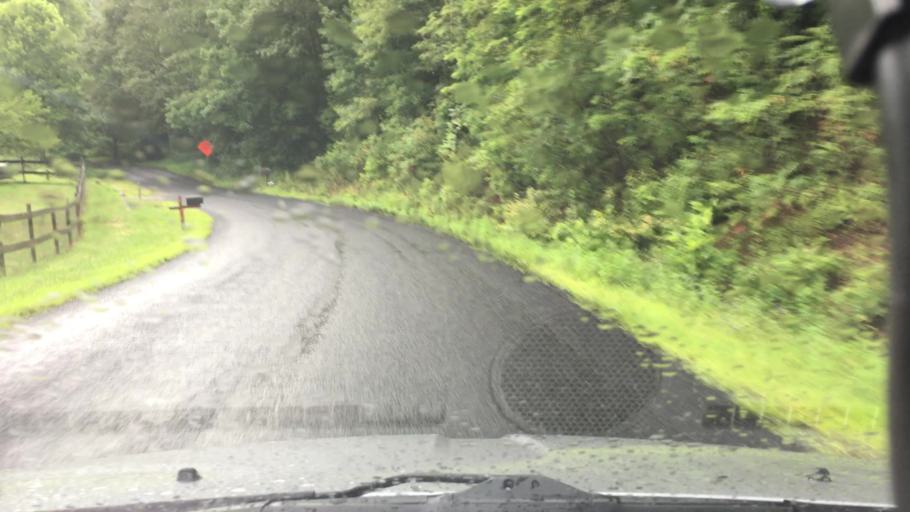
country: US
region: North Carolina
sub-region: Madison County
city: Mars Hill
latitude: 35.9127
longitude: -82.4931
